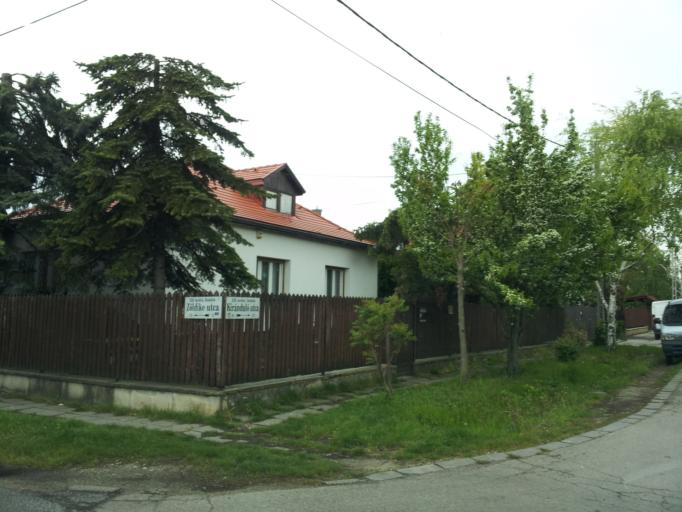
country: HU
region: Budapest
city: Budapest XXII. keruelet
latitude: 47.4292
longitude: 19.0123
